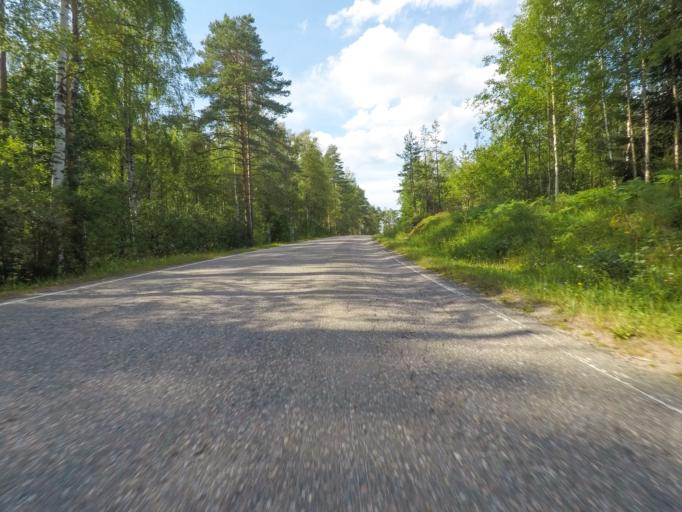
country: FI
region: Southern Savonia
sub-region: Mikkeli
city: Puumala
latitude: 61.6742
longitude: 28.2274
